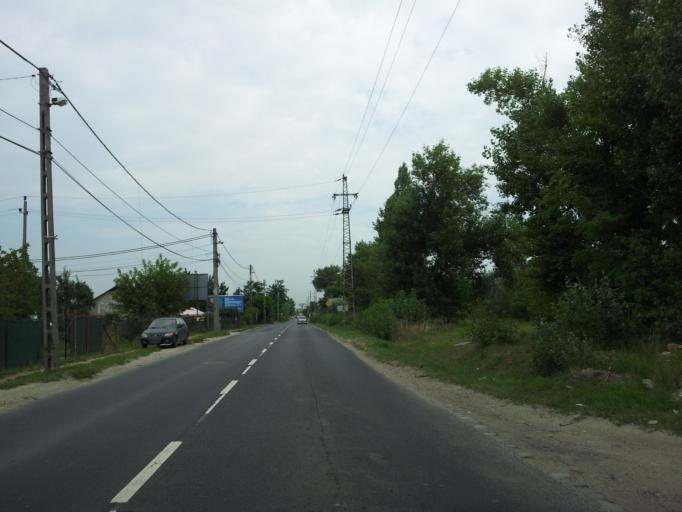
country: HU
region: Budapest
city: Budapest XXII. keruelet
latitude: 47.3921
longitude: 19.0531
